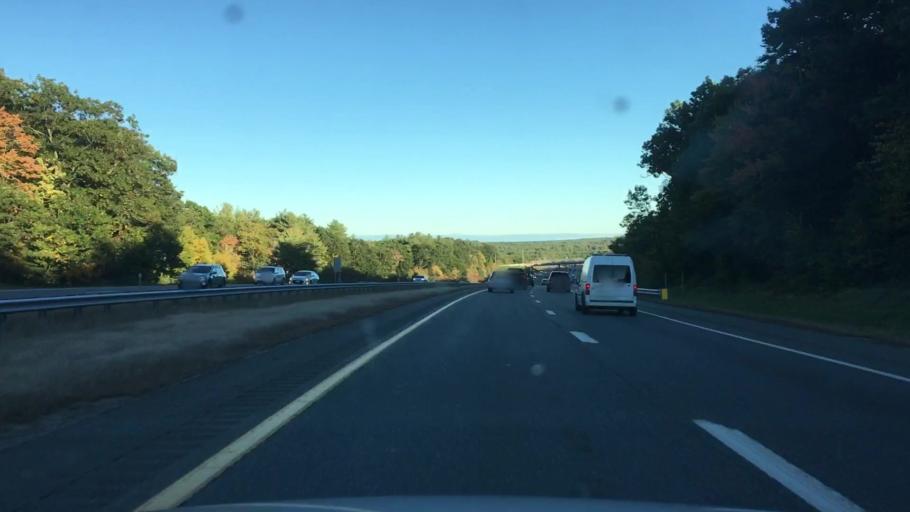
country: US
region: New Hampshire
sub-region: Rockingham County
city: Exeter
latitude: 43.0031
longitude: -70.9568
